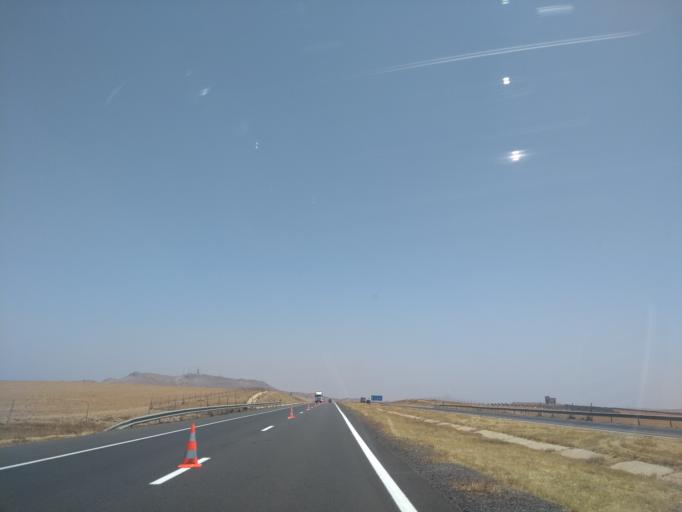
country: MA
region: Marrakech-Tensift-Al Haouz
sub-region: Kelaa-Des-Sraghna
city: Sidi Abdallah
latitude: 32.4428
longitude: -7.9318
